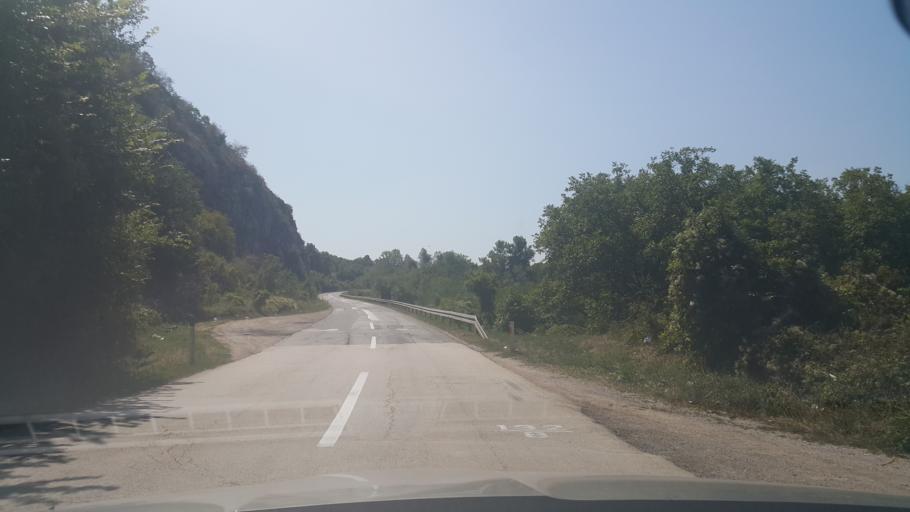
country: RS
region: Central Serbia
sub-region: Zajecarski Okrug
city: Zajecar
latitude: 43.7655
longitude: 22.3103
